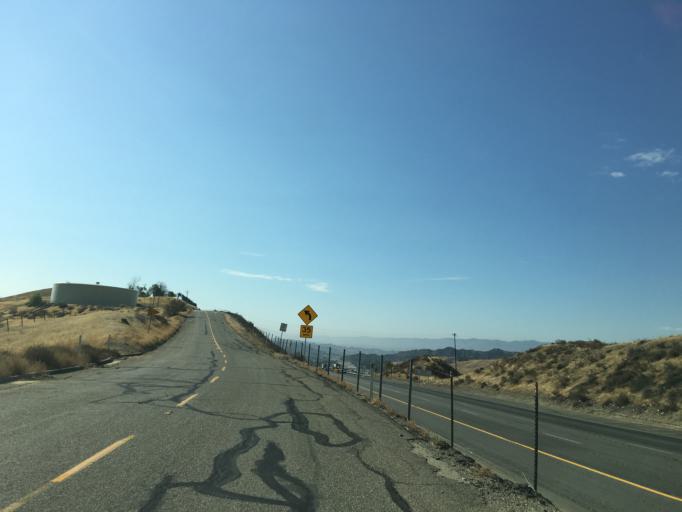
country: US
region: California
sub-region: Los Angeles County
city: Castaic
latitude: 34.5212
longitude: -118.6393
